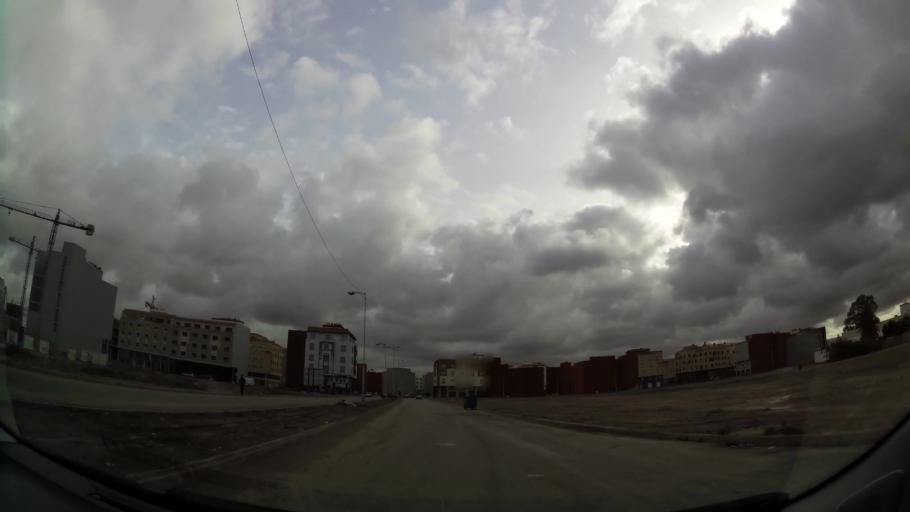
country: MA
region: Oriental
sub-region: Nador
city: Nador
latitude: 35.1559
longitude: -2.9245
